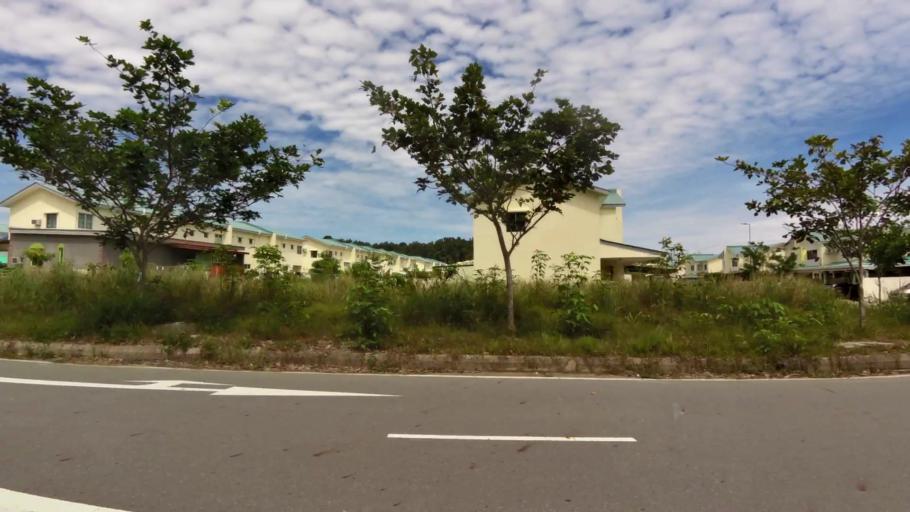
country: BN
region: Brunei and Muara
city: Bandar Seri Begawan
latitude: 4.9815
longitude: 115.0148
